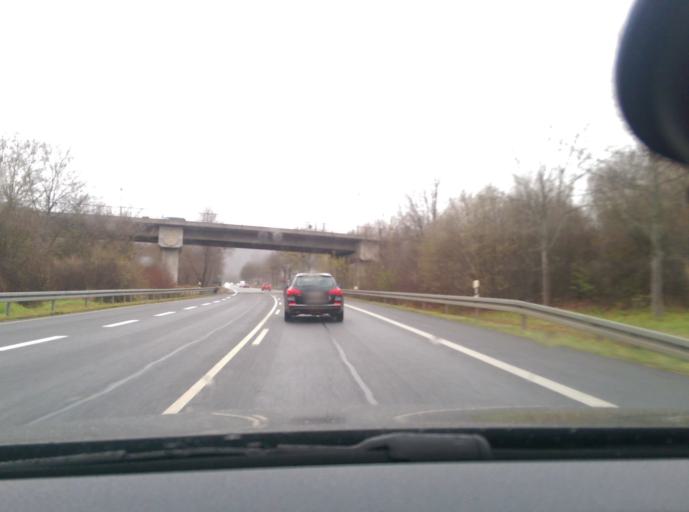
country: DE
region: Hesse
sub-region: Regierungsbezirk Kassel
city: Bad Sooden-Allendorf
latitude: 51.2725
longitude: 9.9674
